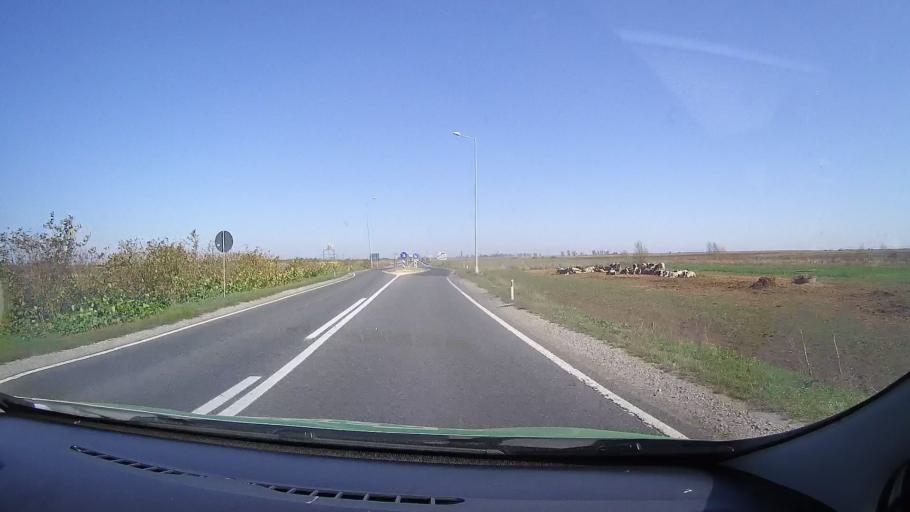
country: RO
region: Satu Mare
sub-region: Comuna Moftinu
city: Moftinu Mic
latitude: 47.6877
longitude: 22.6082
